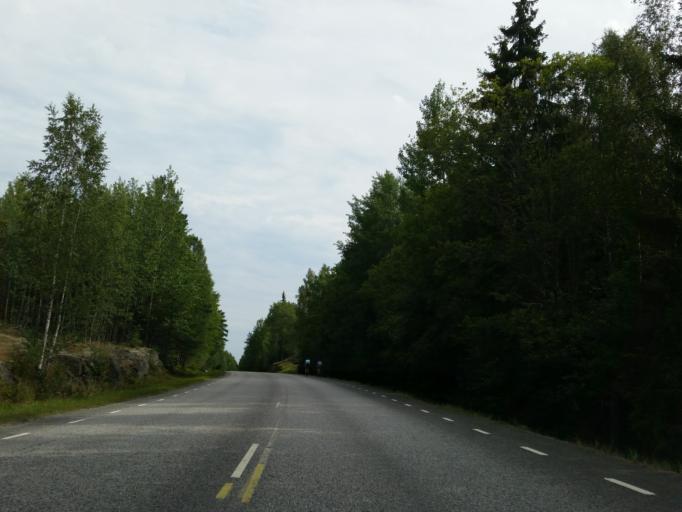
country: SE
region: Soedermanland
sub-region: Strangnas Kommun
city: Mariefred
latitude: 59.2330
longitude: 17.2059
